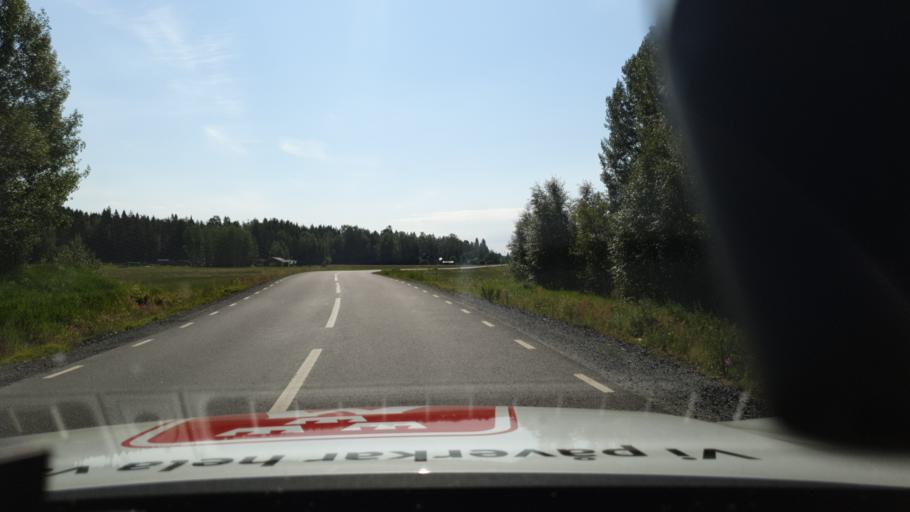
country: SE
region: Norrbotten
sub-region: Lulea Kommun
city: Sodra Sunderbyn
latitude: 65.8190
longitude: 21.9972
